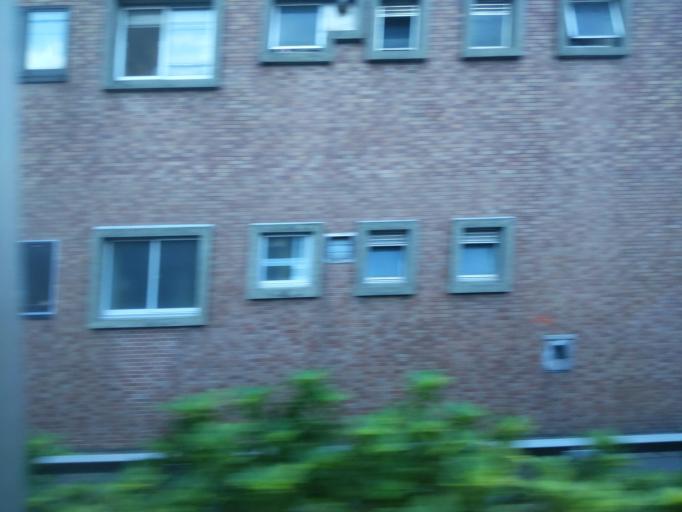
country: JP
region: Tokyo
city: Tokyo
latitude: 35.6795
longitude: 139.6330
